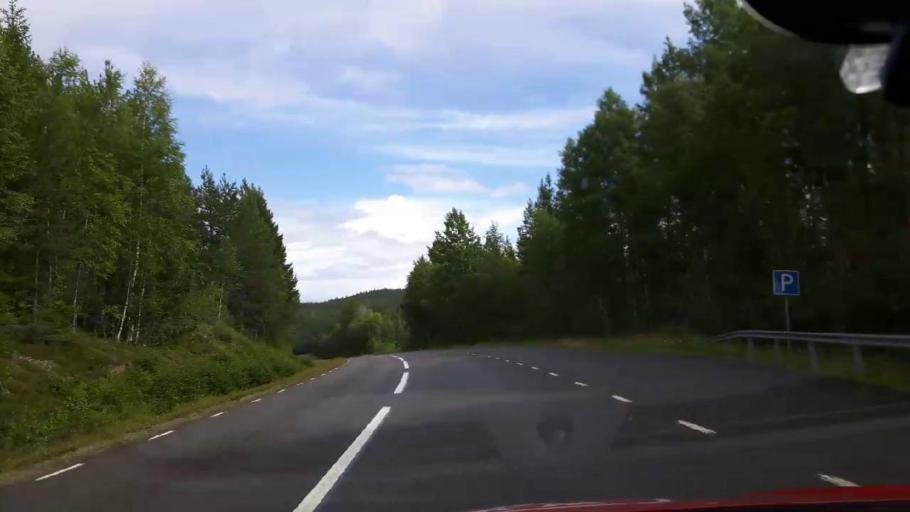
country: SE
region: Jaemtland
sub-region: Stroemsunds Kommun
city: Stroemsund
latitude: 64.3390
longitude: 14.9202
